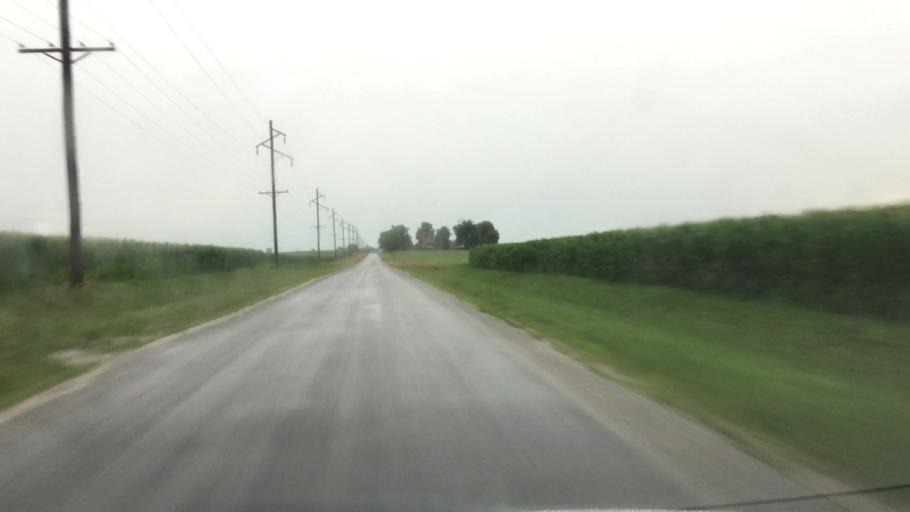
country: US
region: Illinois
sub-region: Hancock County
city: Hamilton
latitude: 40.4553
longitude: -91.2710
